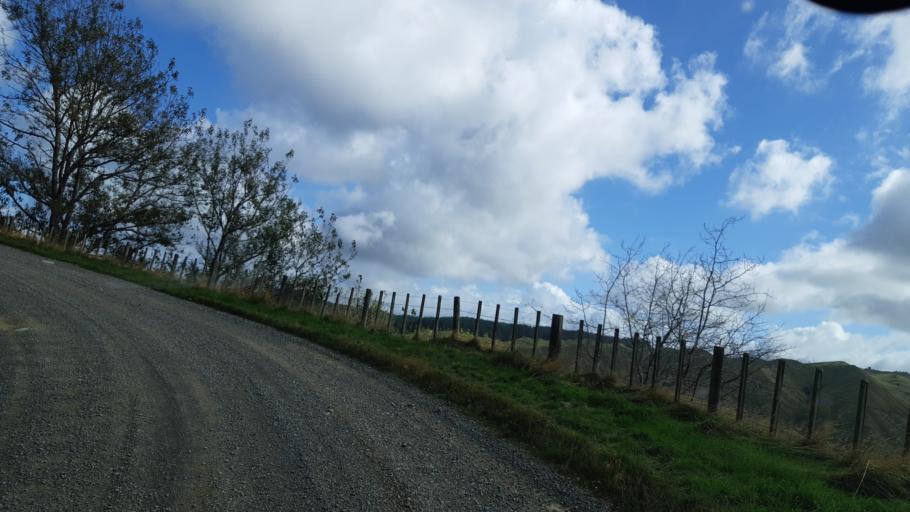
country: NZ
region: Manawatu-Wanganui
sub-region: Ruapehu District
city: Waiouru
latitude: -39.8178
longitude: 175.6613
